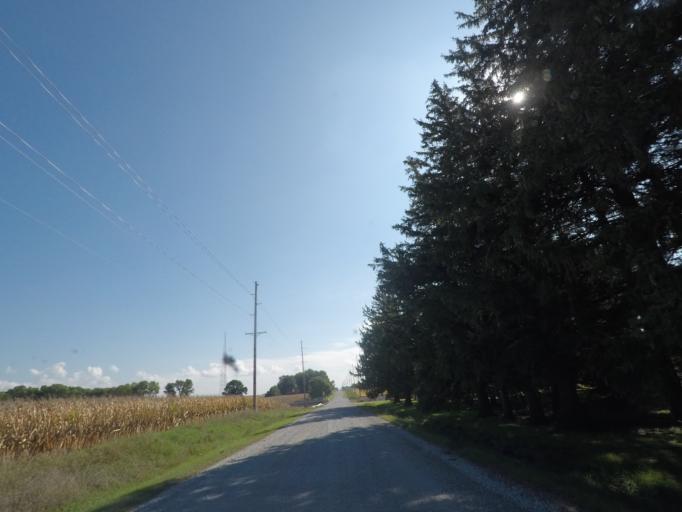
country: US
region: Iowa
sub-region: Story County
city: Nevada
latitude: 42.0344
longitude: -93.3964
